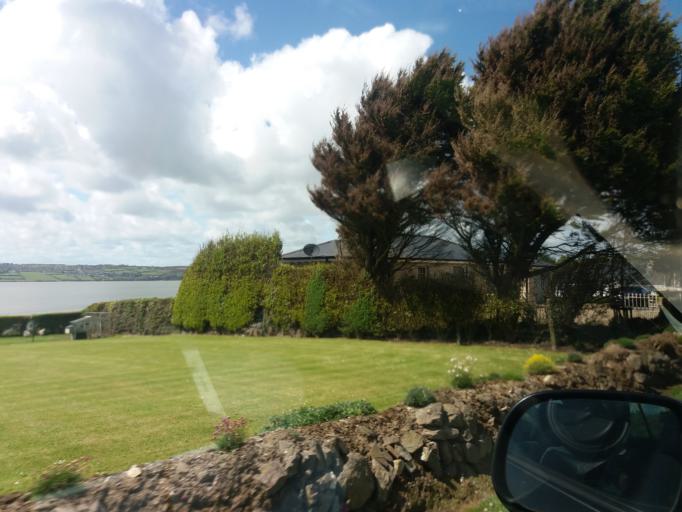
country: IE
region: Munster
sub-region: Waterford
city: Dunmore East
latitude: 52.2266
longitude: -6.9327
